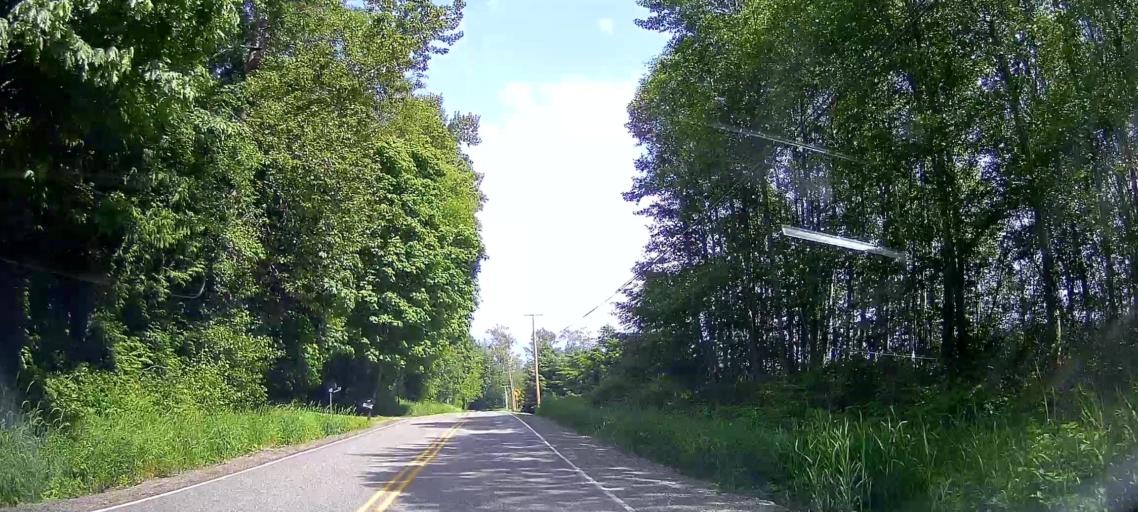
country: US
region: Washington
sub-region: Skagit County
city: Burlington
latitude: 48.5712
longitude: -122.3938
